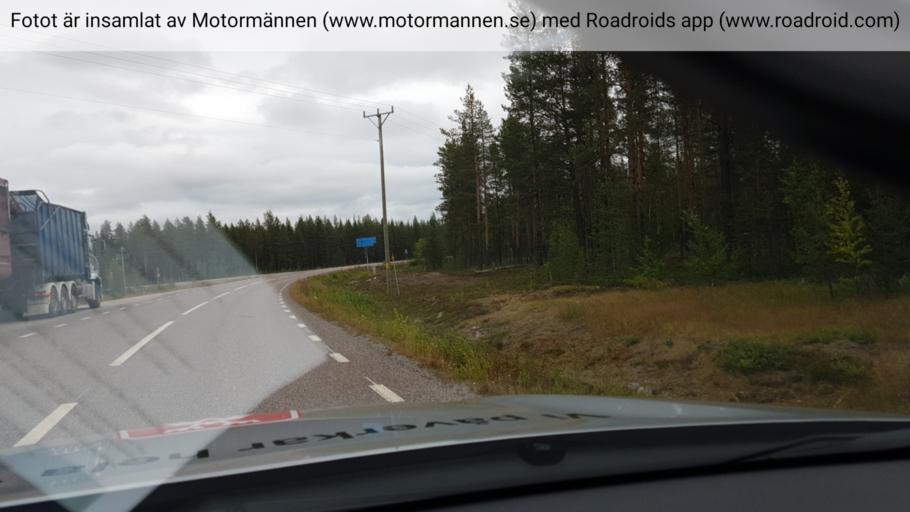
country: SE
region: Norrbotten
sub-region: Gallivare Kommun
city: Gaellivare
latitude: 67.0764
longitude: 21.3354
